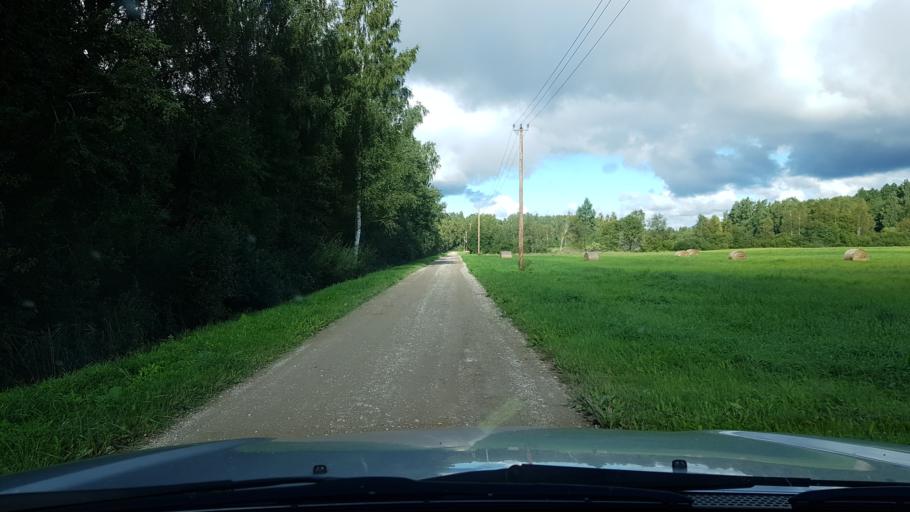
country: EE
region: Harju
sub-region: Rae vald
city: Vaida
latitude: 59.2525
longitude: 25.0622
